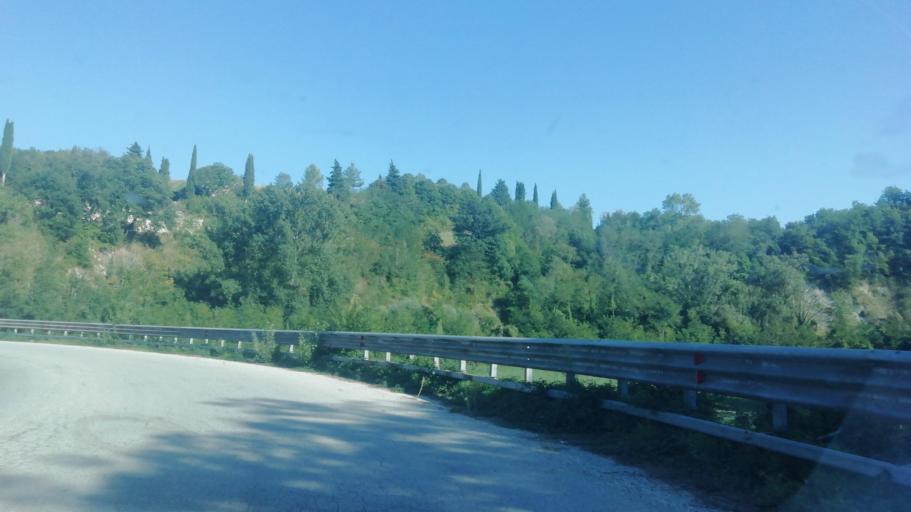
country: IT
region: The Marches
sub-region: Provincia di Pesaro e Urbino
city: Pergola
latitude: 43.5599
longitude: 12.8275
